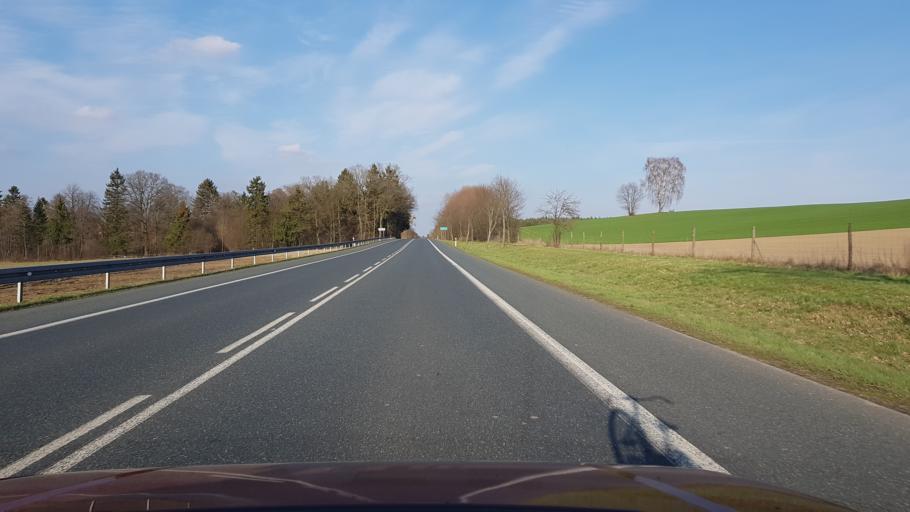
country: PL
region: West Pomeranian Voivodeship
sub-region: Powiat kolobrzeski
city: Ryman
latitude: 53.9091
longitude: 15.4411
